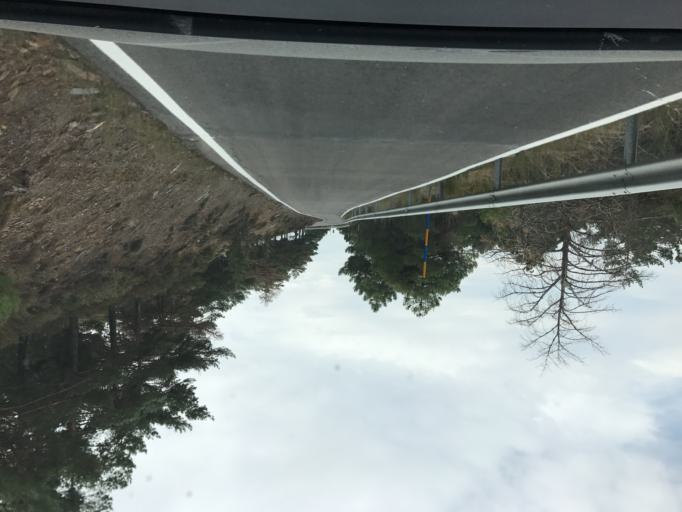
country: ES
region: Andalusia
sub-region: Provincia de Granada
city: Aldeire
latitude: 37.1354
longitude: -3.0443
